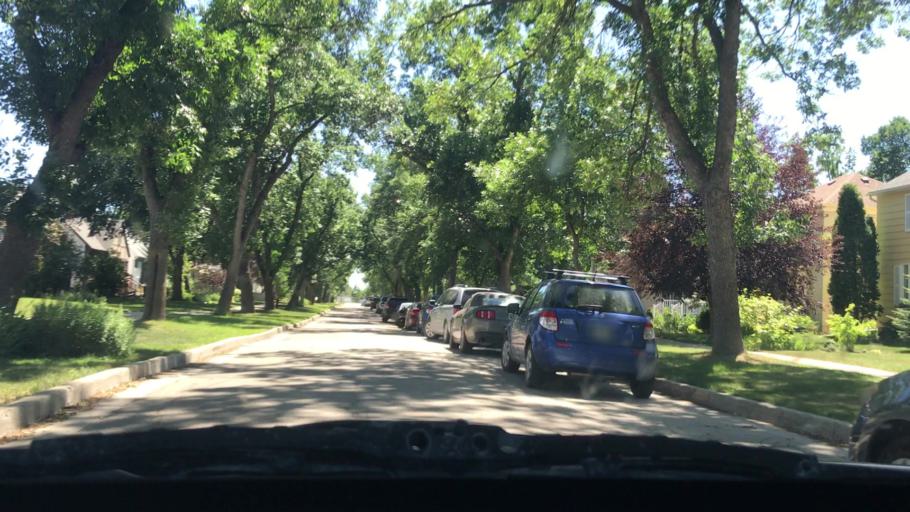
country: CA
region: Manitoba
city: Winnipeg
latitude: 49.8700
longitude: -97.1960
